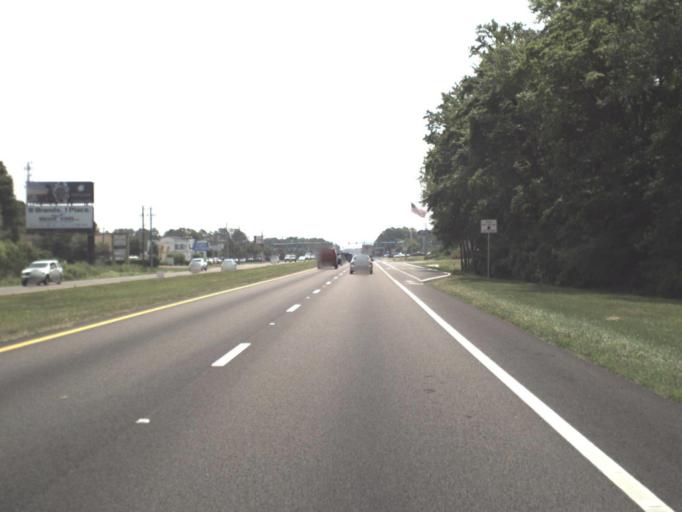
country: US
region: Florida
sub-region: Nassau County
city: Yulee
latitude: 30.6231
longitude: -81.5365
